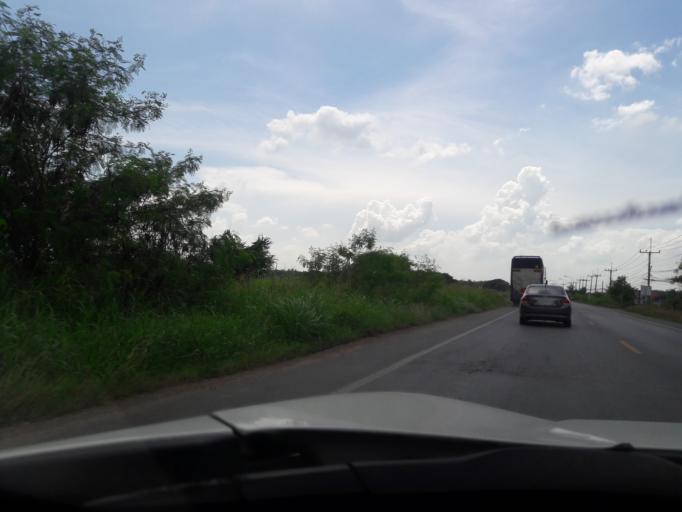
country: TH
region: Phra Nakhon Si Ayutthaya
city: Ban Phraek
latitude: 14.6325
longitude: 100.5623
